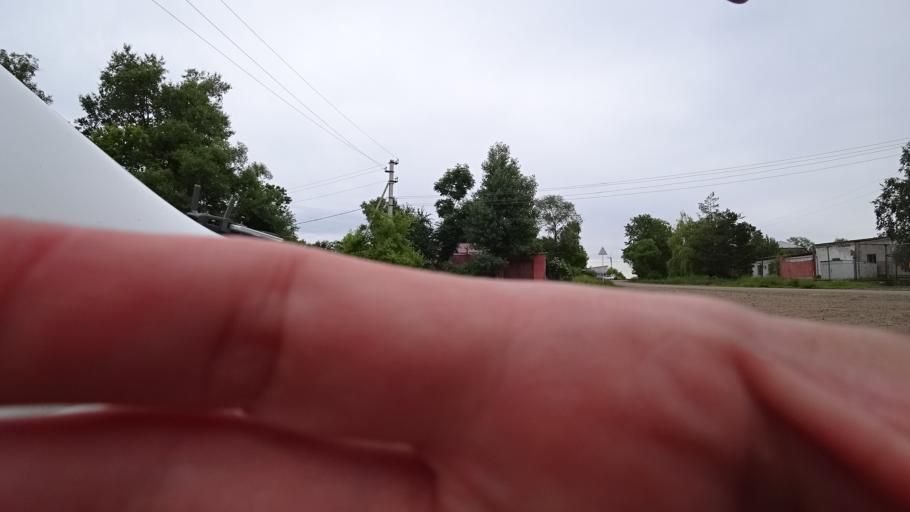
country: RU
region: Primorskiy
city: Novosysoyevka
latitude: 44.2123
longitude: 133.3410
